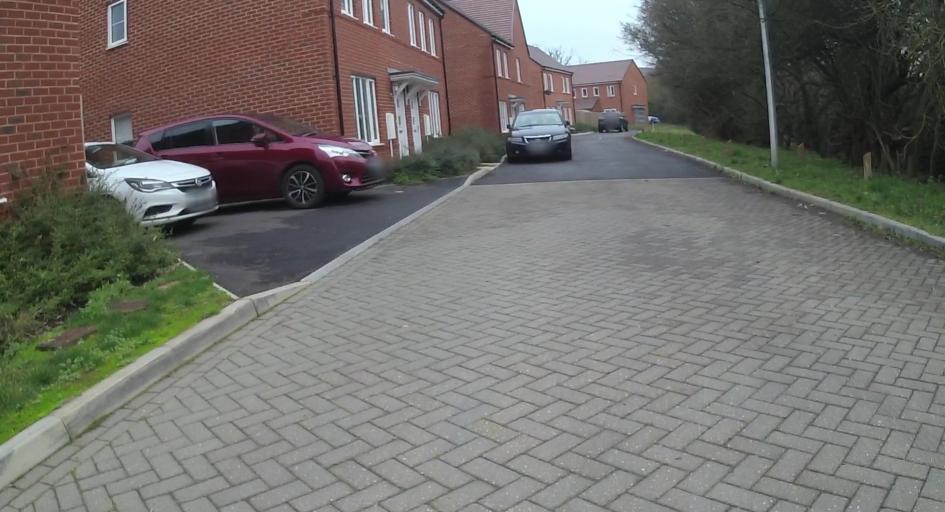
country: GB
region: England
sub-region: Wokingham
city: Wokingham
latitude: 51.4082
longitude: -0.8102
